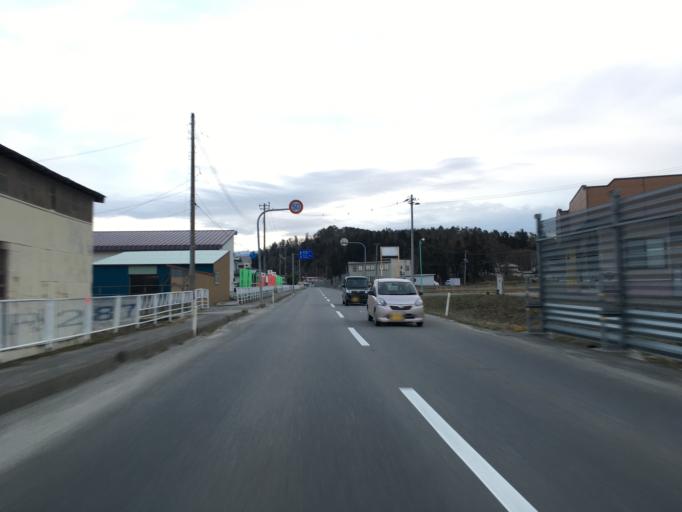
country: JP
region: Yamagata
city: Yonezawa
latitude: 37.9487
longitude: 140.0720
